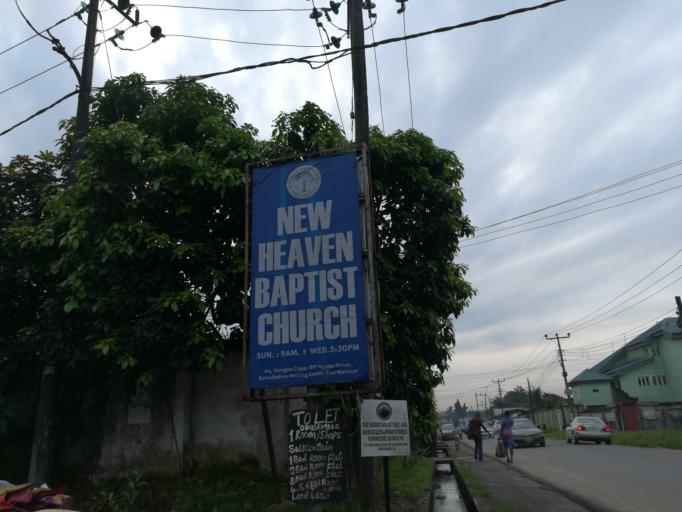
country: NG
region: Rivers
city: Port Harcourt
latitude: 4.8459
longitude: 7.0470
